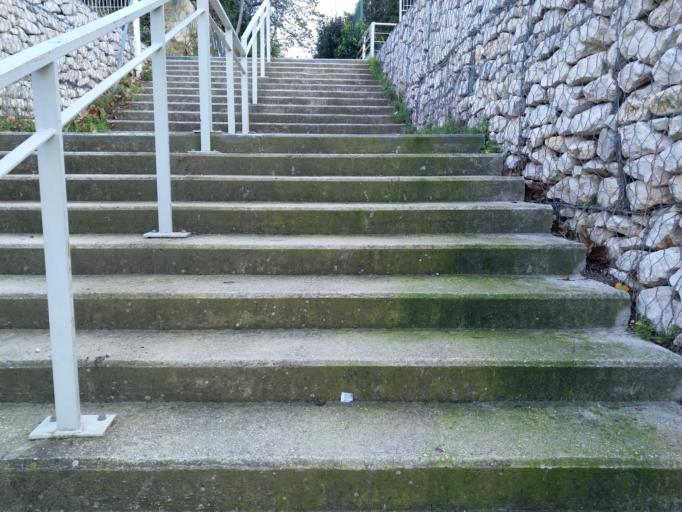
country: FR
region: Provence-Alpes-Cote d'Azur
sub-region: Departement des Bouches-du-Rhone
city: Marseille 13
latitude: 43.3189
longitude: 5.4227
